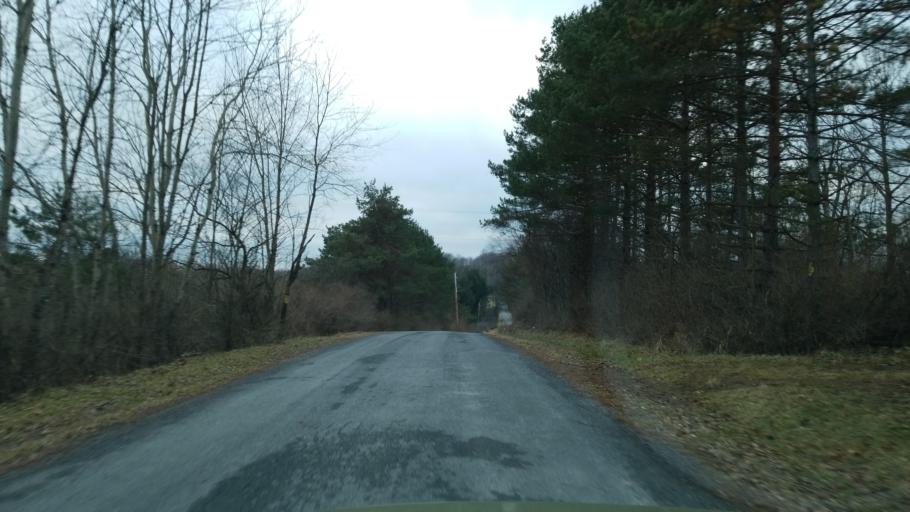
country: US
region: Pennsylvania
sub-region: Jefferson County
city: Falls Creek
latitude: 41.1802
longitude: -78.8081
